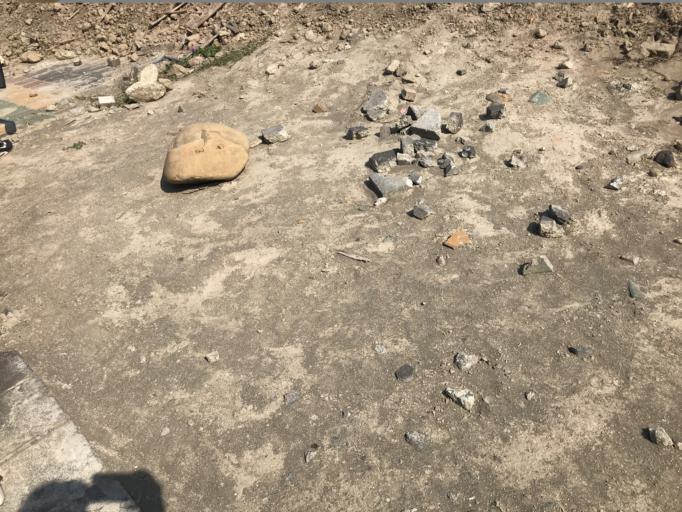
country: TW
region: Taiwan
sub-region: Hsinchu
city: Hsinchu
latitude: 24.8510
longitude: 120.9290
